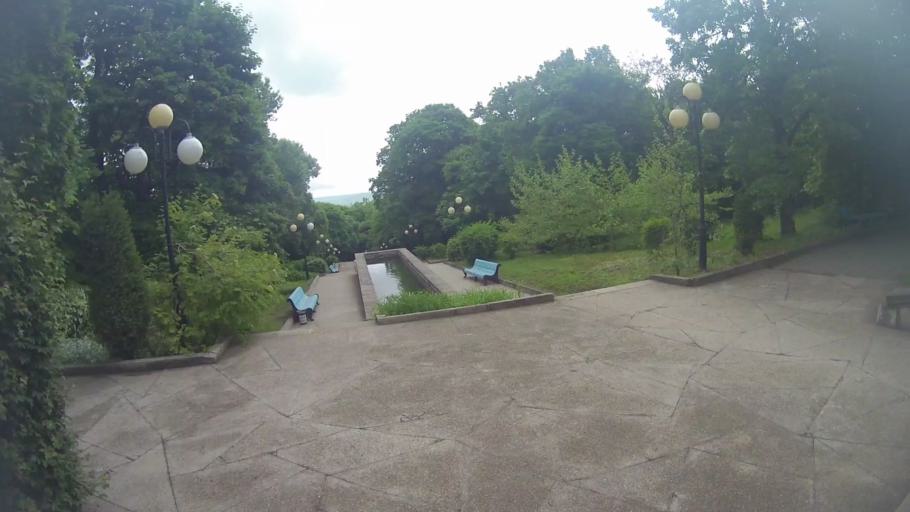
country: RU
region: Stavropol'skiy
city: Zheleznovodsk
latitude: 44.1373
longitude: 43.0365
